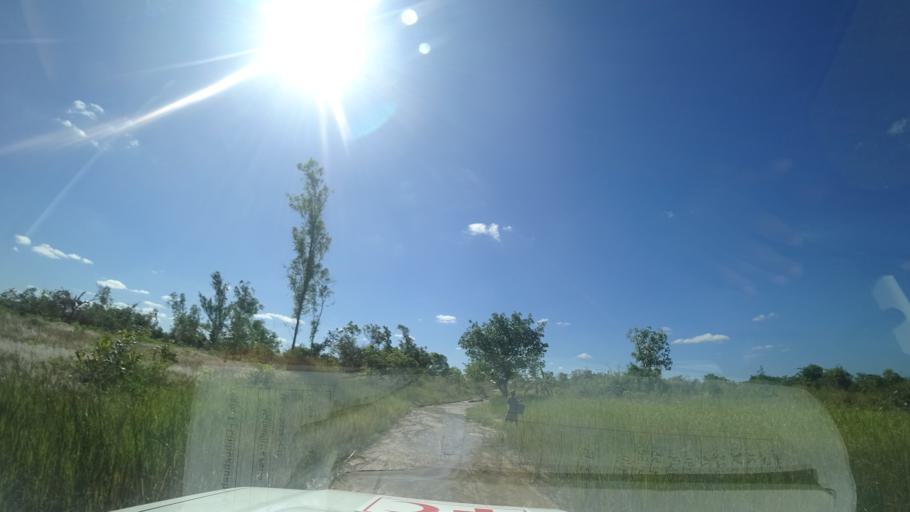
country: MZ
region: Sofala
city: Dondo
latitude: -19.4758
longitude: 34.6298
